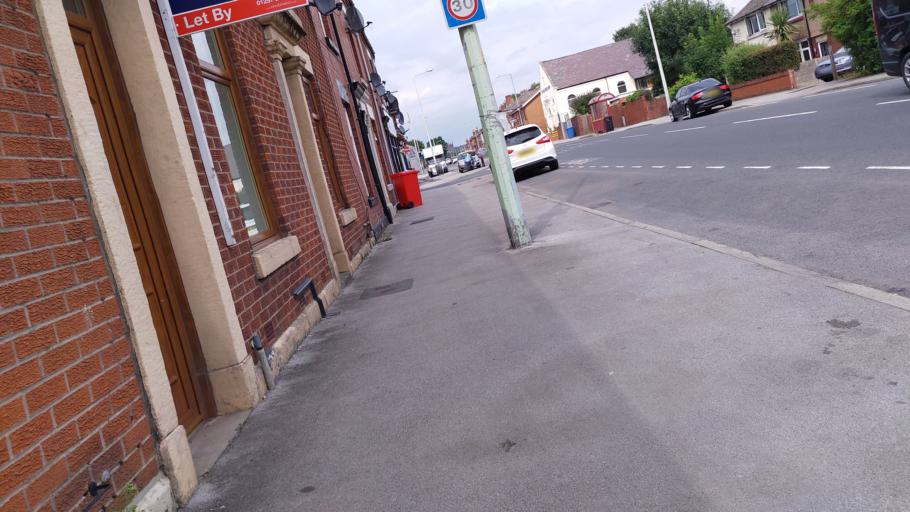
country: GB
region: England
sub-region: Lancashire
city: Chorley
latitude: 53.6427
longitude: -2.6385
